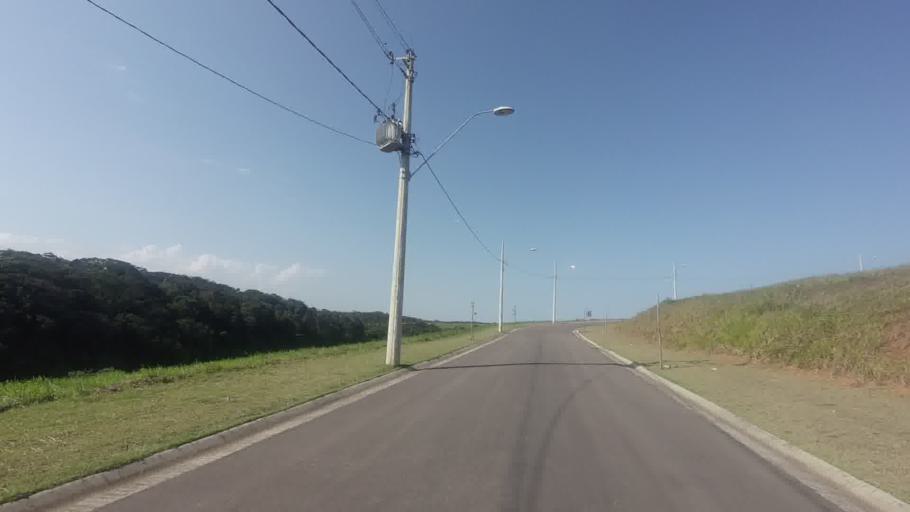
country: BR
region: Espirito Santo
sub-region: Guarapari
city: Guarapari
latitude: -20.7111
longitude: -40.5315
